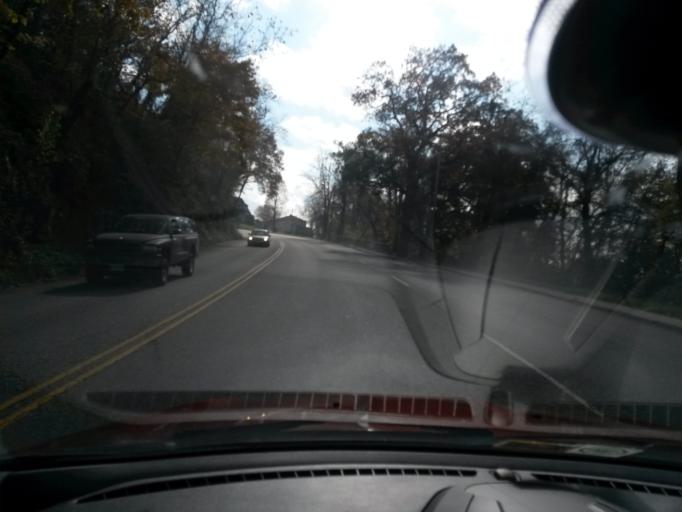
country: US
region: Virginia
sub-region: City of Covington
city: Fairlawn
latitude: 37.7796
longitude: -79.9868
